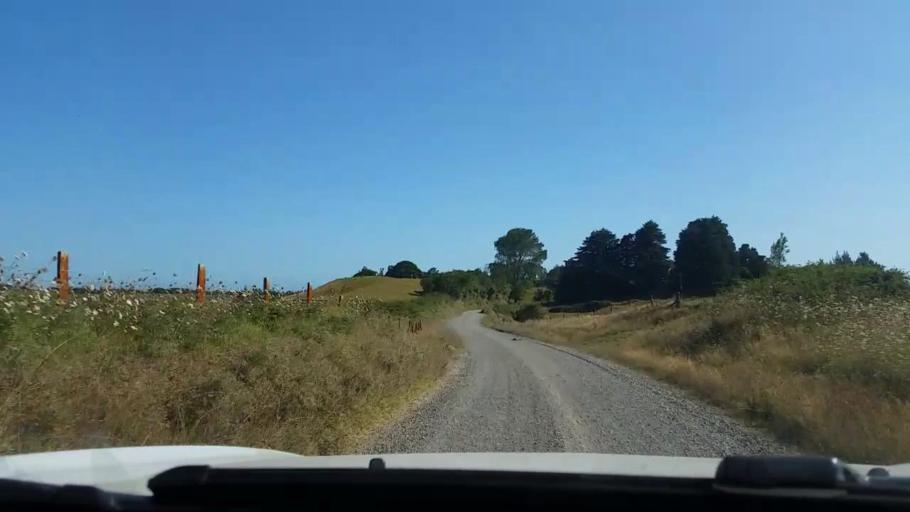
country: NZ
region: Bay of Plenty
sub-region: Western Bay of Plenty District
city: Maketu
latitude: -37.9637
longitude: 176.4353
